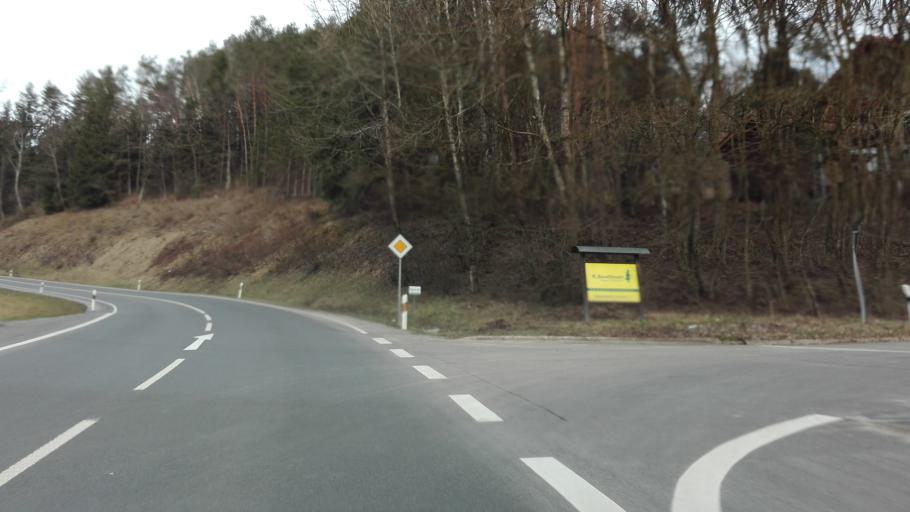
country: DE
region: Bavaria
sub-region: Lower Bavaria
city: Thyrnau
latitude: 48.6272
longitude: 13.5717
